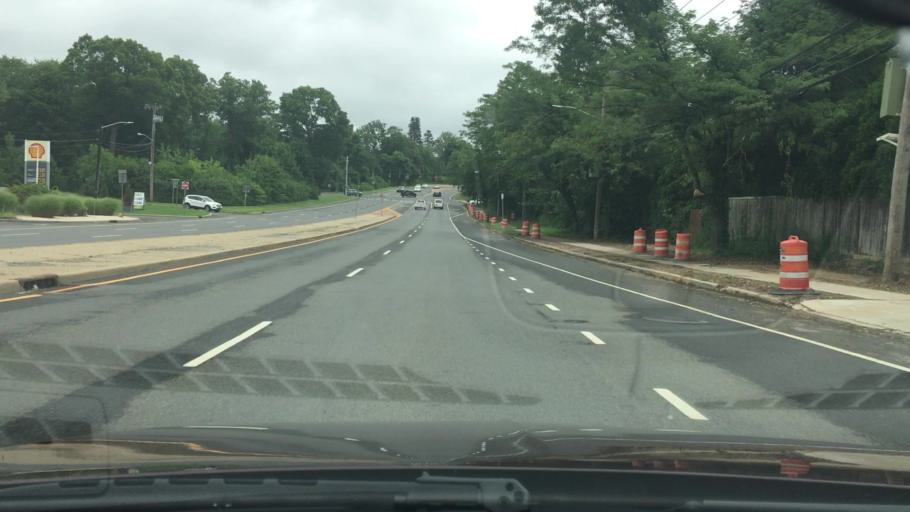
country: US
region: New York
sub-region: Nassau County
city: Jericho
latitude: 40.7960
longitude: -73.5343
